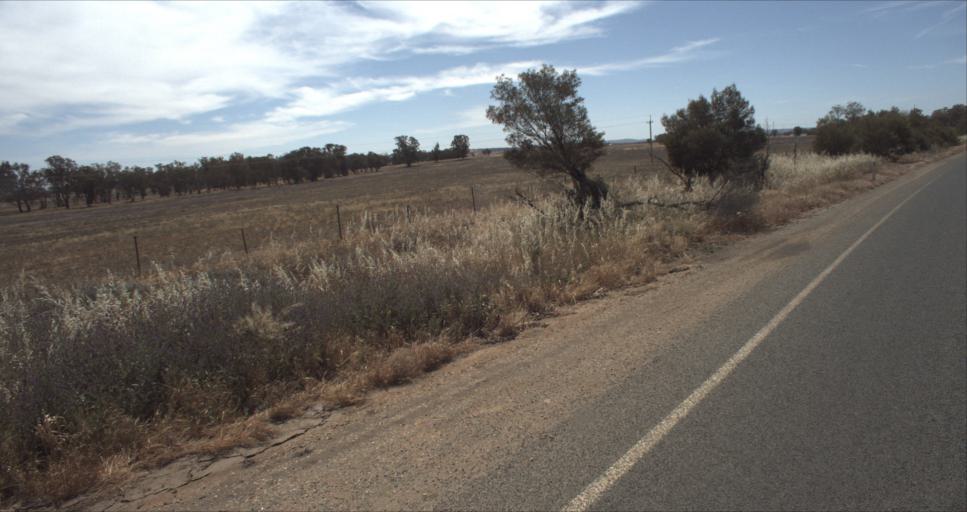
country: AU
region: New South Wales
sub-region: Leeton
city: Leeton
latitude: -34.6621
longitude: 146.4501
